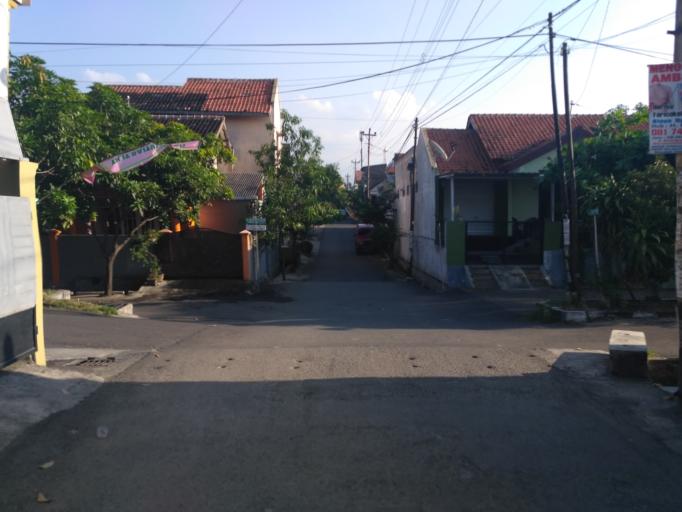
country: ID
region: Central Java
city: Mranggen
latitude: -7.0202
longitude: 110.4666
